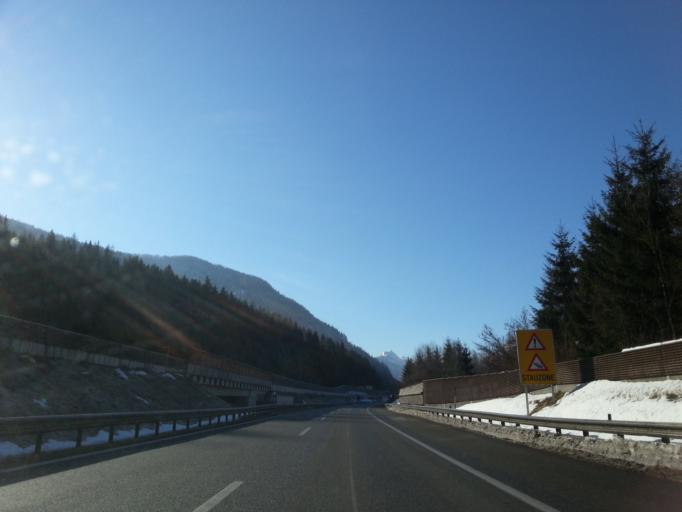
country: AT
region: Salzburg
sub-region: Politischer Bezirk Sankt Johann im Pongau
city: Flachau
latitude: 47.3600
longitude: 13.3976
